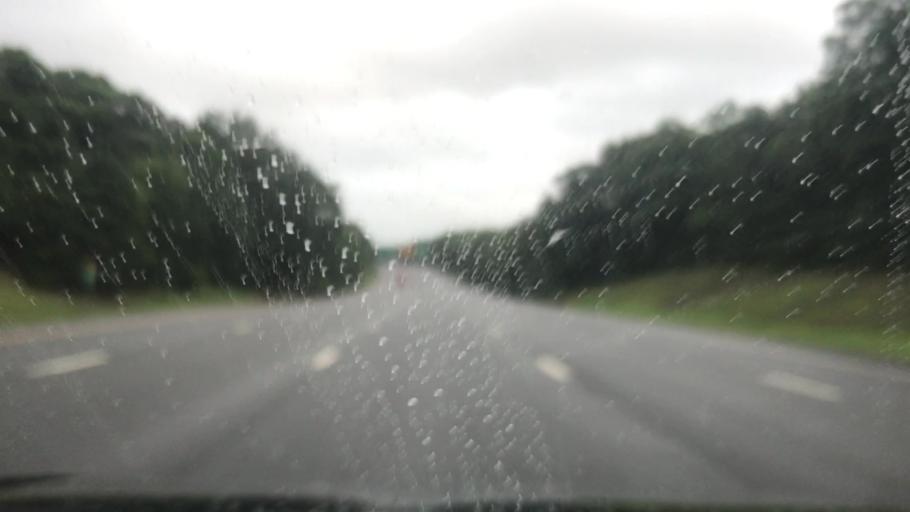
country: US
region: New Jersey
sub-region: Monmouth County
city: Shark River Hills
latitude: 40.2424
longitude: -74.0850
